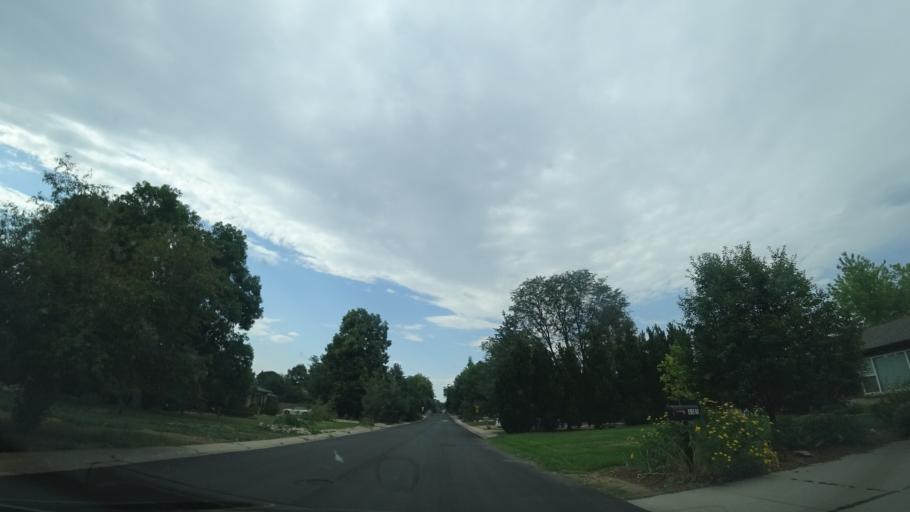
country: US
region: Colorado
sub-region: Jefferson County
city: Lakewood
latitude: 39.7153
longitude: -105.0874
